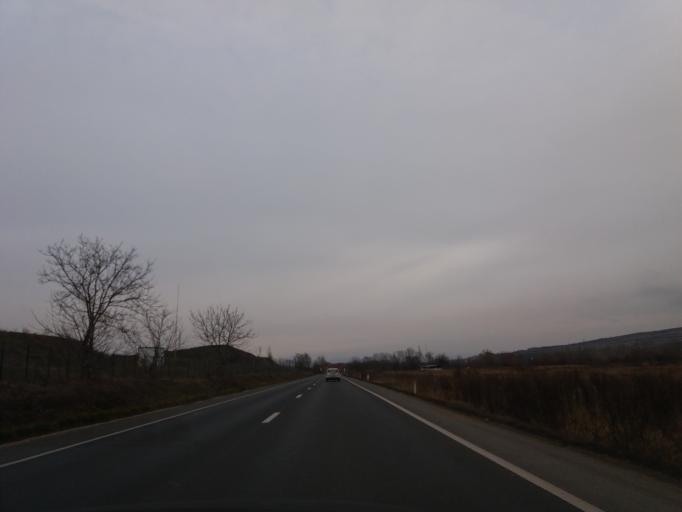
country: RO
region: Hunedoara
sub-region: Comuna Calan
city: Calan
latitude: 45.7462
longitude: 23.0001
